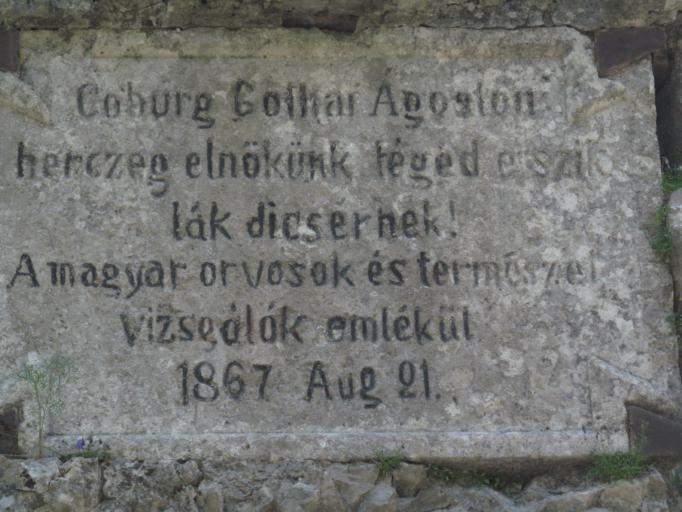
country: SK
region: Kosicky
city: Dobsina
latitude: 48.8733
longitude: 20.3292
